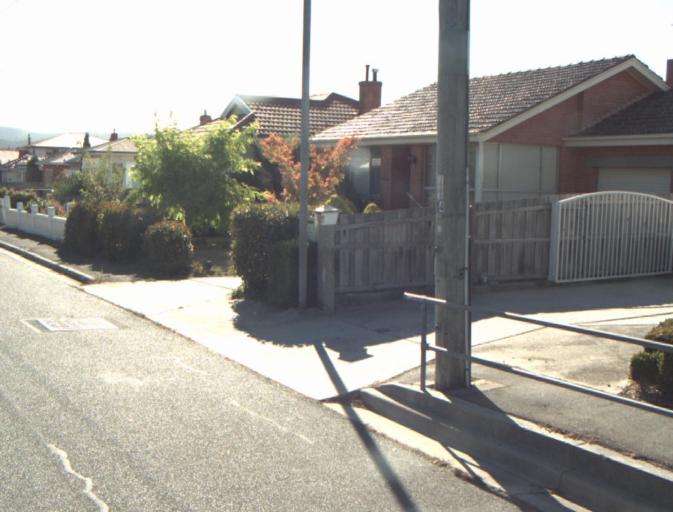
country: AU
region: Tasmania
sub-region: Launceston
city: Newnham
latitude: -41.4057
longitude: 147.1253
